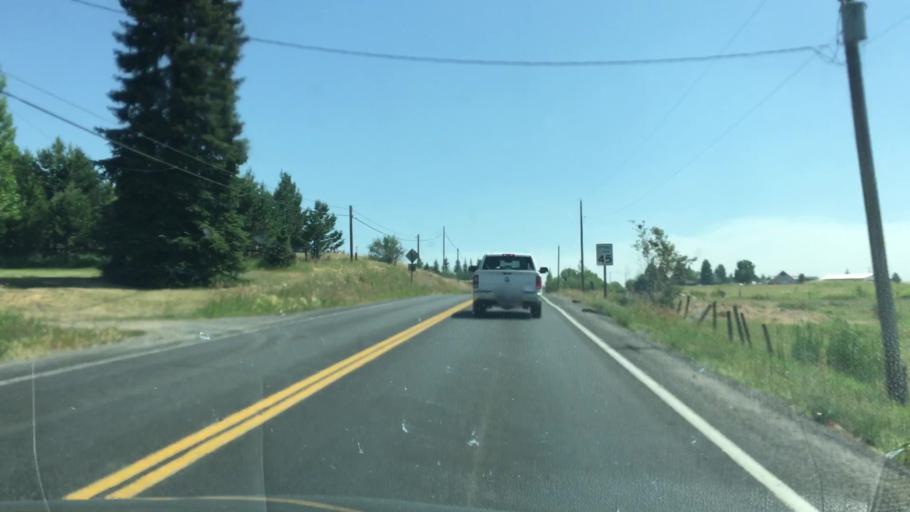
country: US
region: Idaho
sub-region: Valley County
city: McCall
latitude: 44.8883
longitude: -116.0925
